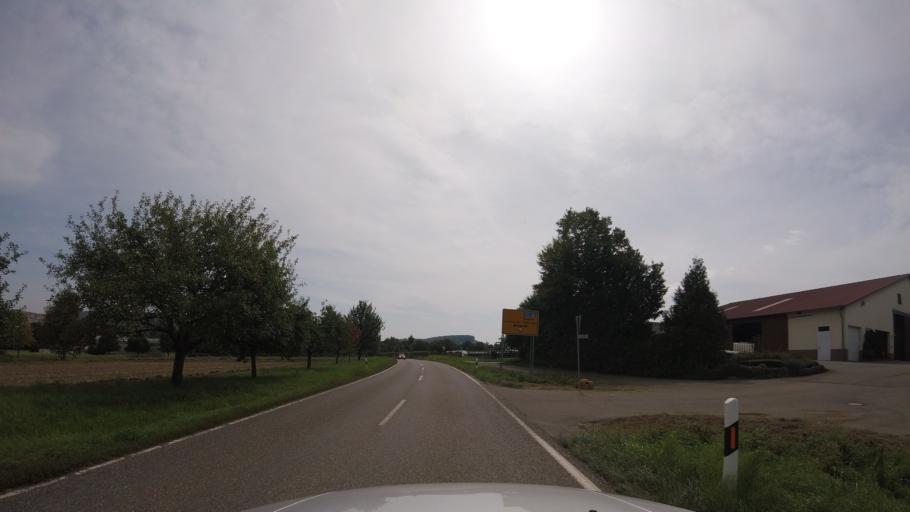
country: DE
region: Baden-Wuerttemberg
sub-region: Regierungsbezirk Stuttgart
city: Grossbottwar
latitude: 49.0048
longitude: 9.2829
